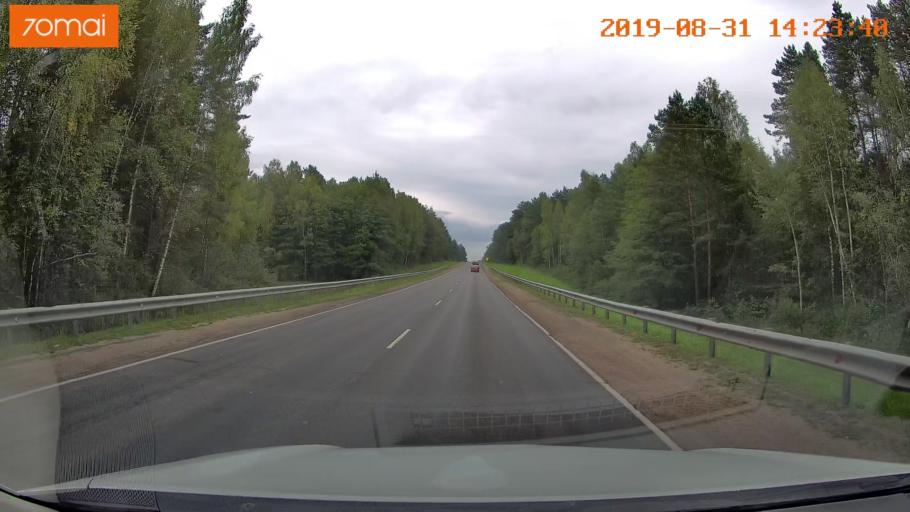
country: RU
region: Smolensk
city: Yekimovichi
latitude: 54.0979
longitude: 33.2385
